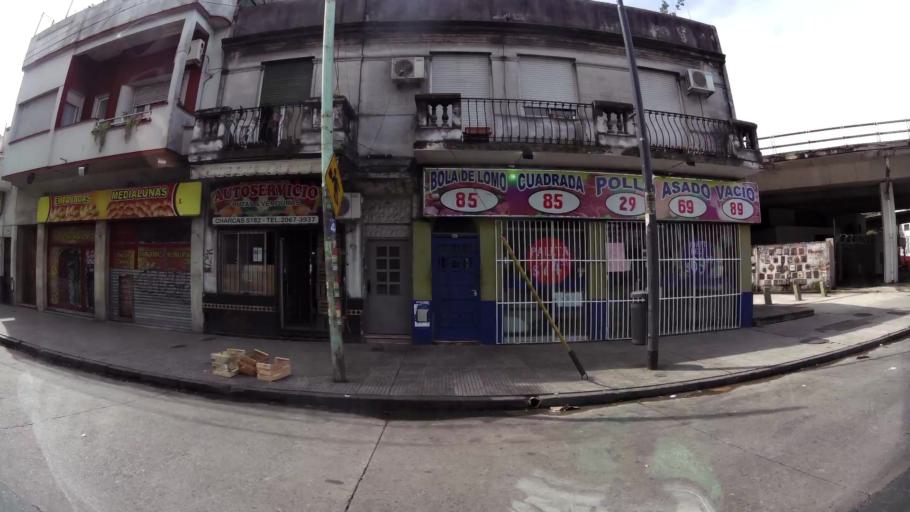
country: AR
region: Buenos Aires F.D.
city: Villa Santa Rita
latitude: -34.6370
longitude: -58.4960
